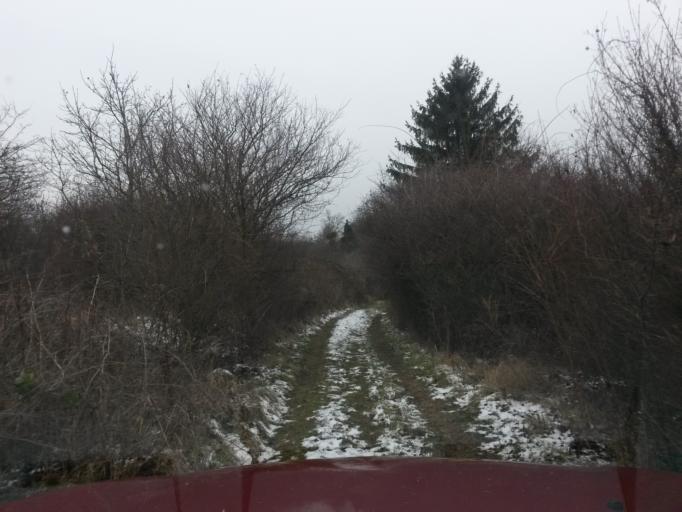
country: SK
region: Kosicky
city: Kosice
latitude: 48.7209
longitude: 21.2831
